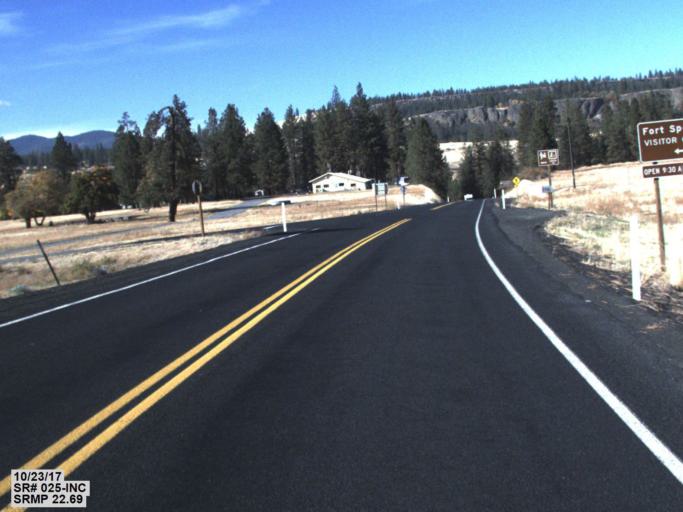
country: US
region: Washington
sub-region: Lincoln County
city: Davenport
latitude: 47.9043
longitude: -118.3041
